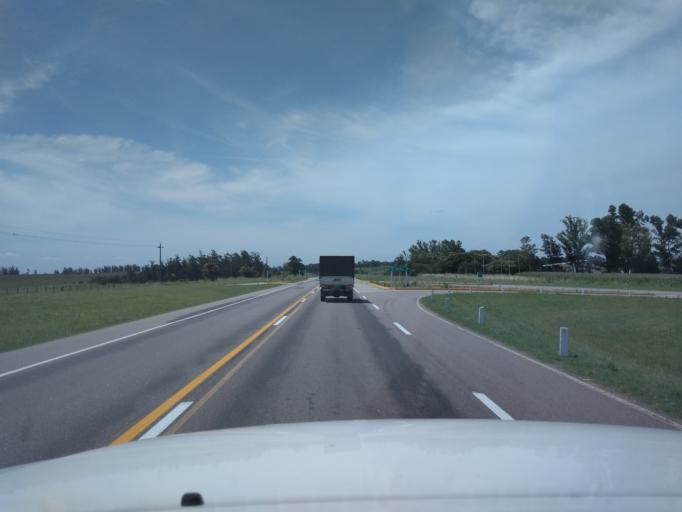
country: UY
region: Florida
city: Florida
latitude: -34.1352
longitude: -56.1837
